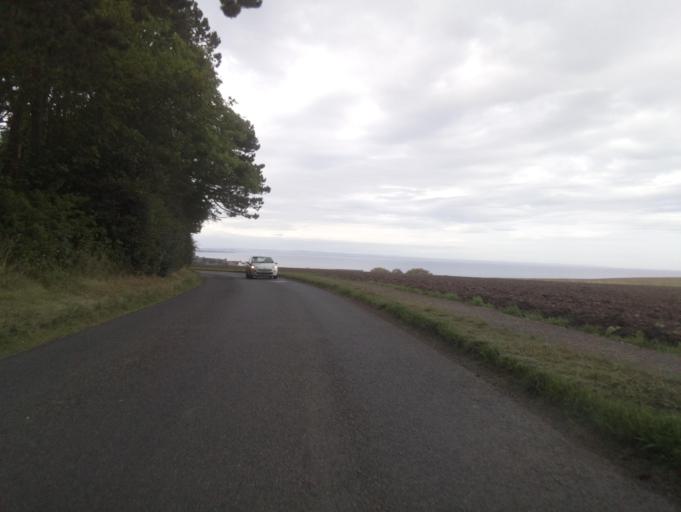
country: GB
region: Scotland
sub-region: Fife
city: Saint Andrews
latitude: 56.3273
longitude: -2.7817
